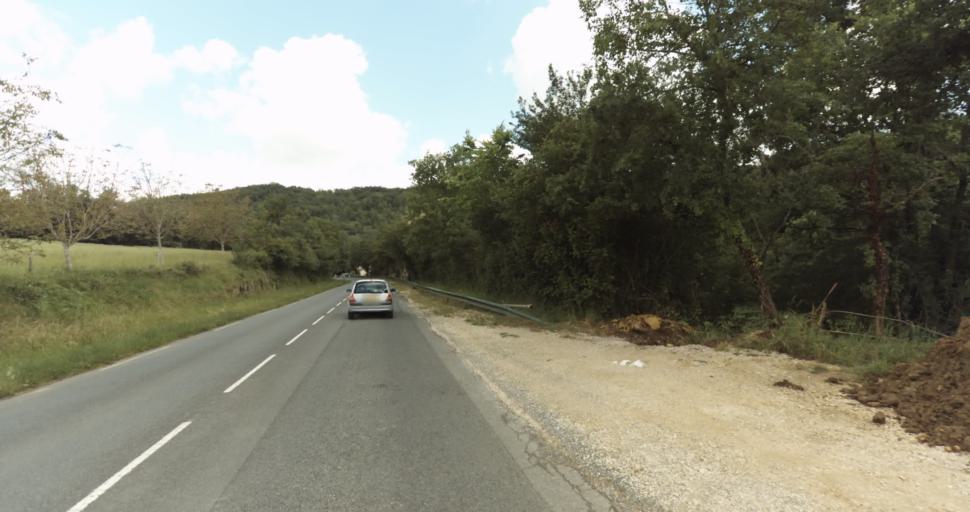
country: FR
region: Aquitaine
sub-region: Departement de la Dordogne
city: Beaumont-du-Perigord
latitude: 44.7835
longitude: 0.7662
